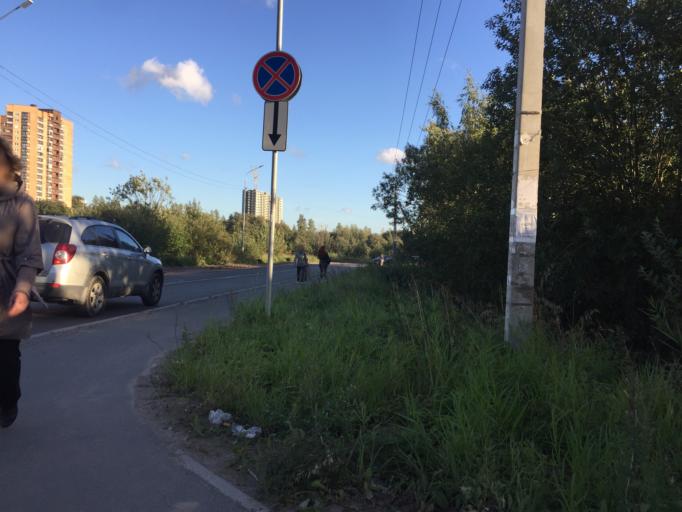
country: RU
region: Leningrad
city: Murino
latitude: 60.0574
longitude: 30.4595
